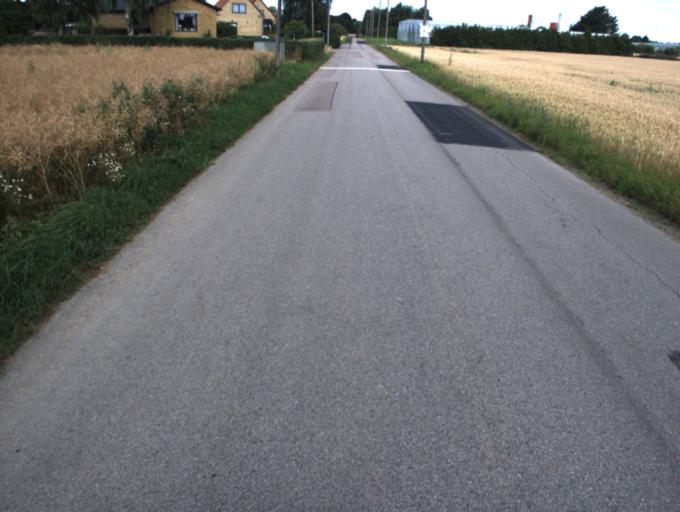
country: SE
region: Skane
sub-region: Helsingborg
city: Gantofta
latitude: 56.0078
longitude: 12.7878
